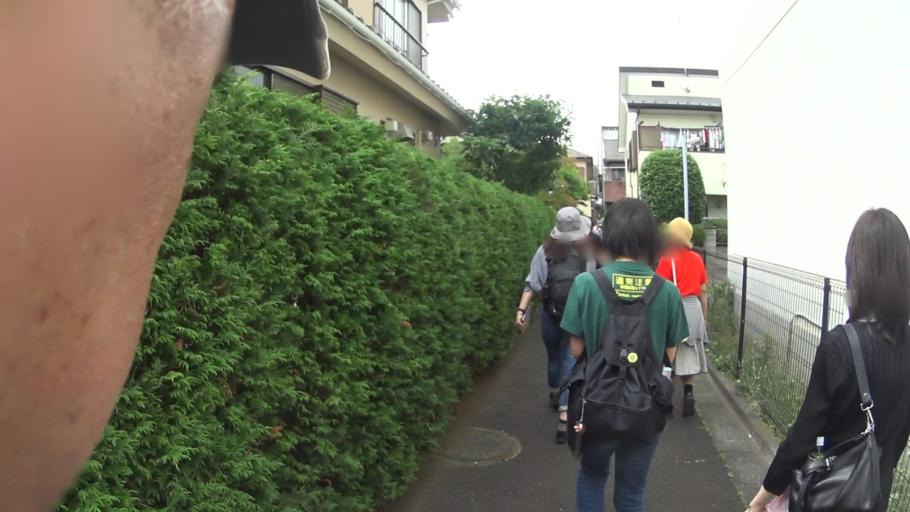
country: JP
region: Tokyo
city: Musashino
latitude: 35.7156
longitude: 139.6035
